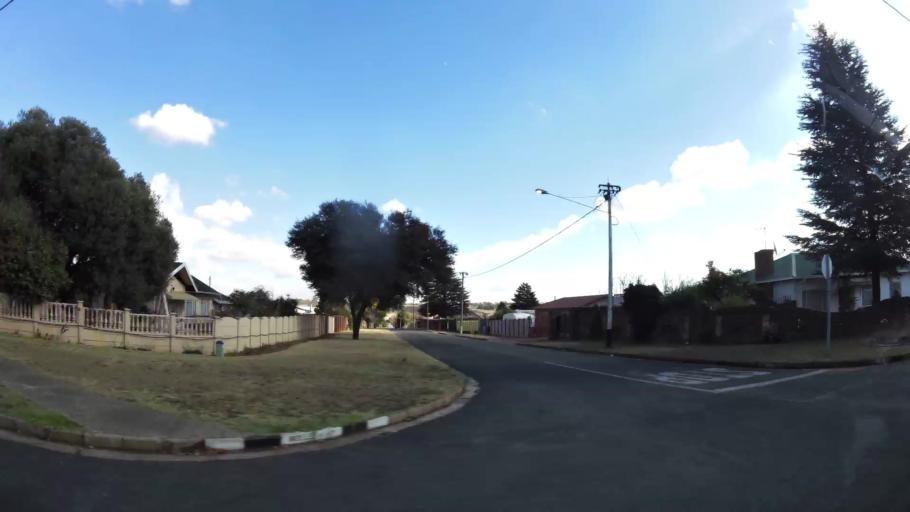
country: ZA
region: Gauteng
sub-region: City of Johannesburg Metropolitan Municipality
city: Roodepoort
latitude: -26.1365
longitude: 27.8298
